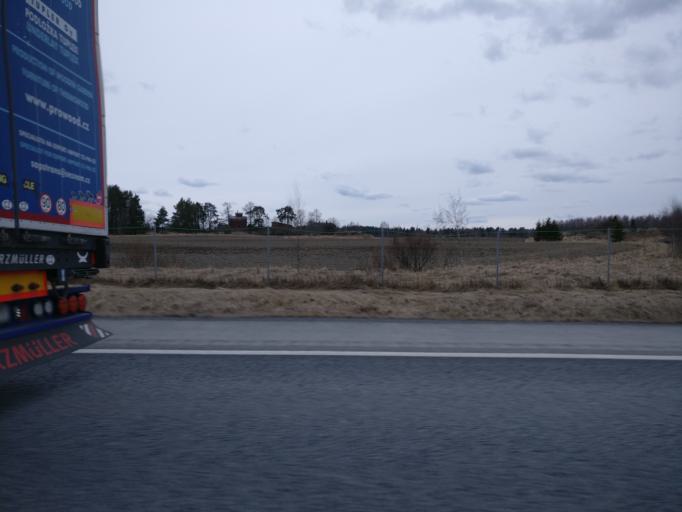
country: FI
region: Pirkanmaa
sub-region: Etelae-Pirkanmaa
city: Akaa
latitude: 61.1921
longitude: 23.8653
